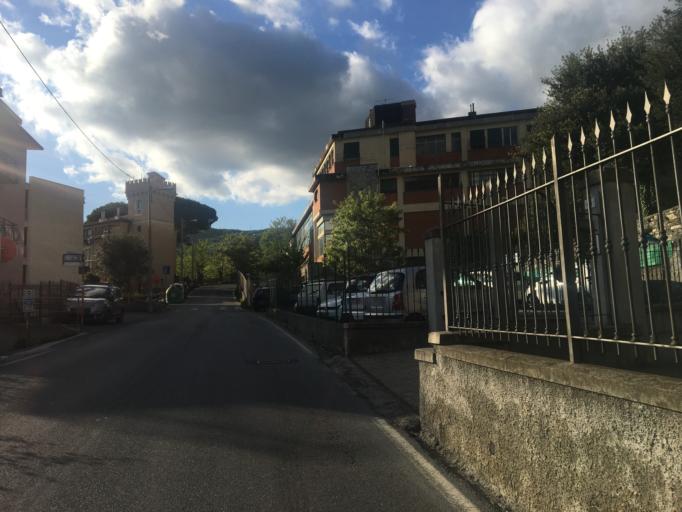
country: IT
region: Liguria
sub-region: Provincia di Genova
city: Piccarello
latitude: 44.4569
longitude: 8.9828
